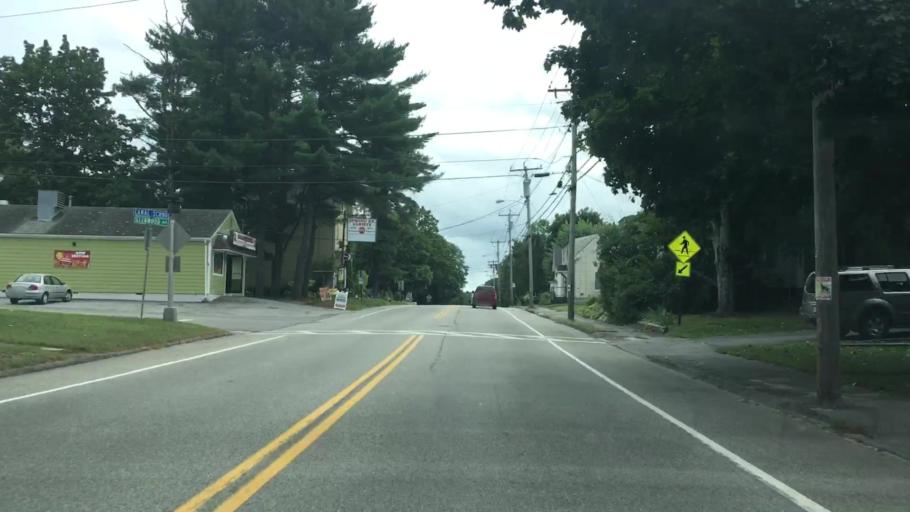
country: US
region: Maine
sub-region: Cumberland County
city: Westbrook
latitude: 43.6716
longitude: -70.3612
